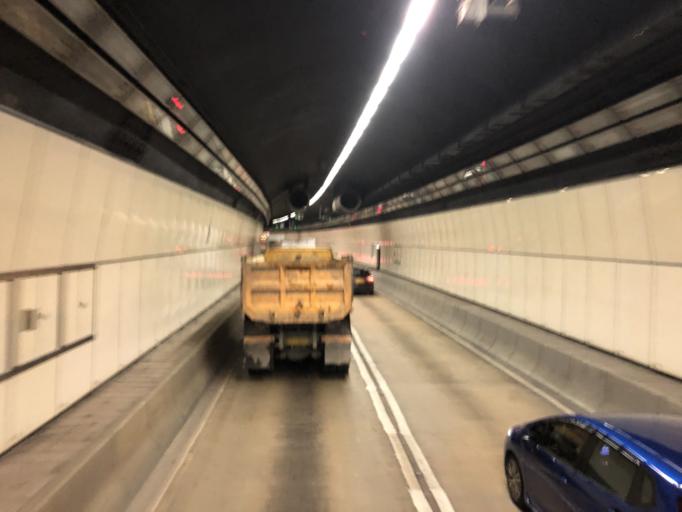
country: HK
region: Sai Kung
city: Sai Kung
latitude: 22.3208
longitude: 114.2498
